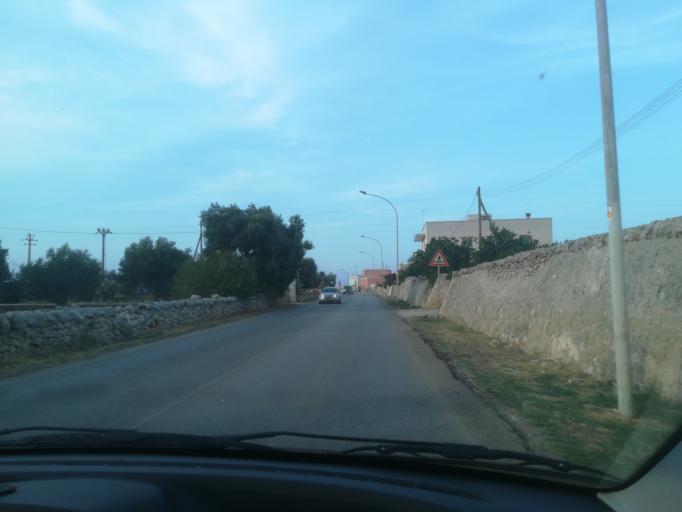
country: IT
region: Apulia
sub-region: Provincia di Bari
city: Monopoli
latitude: 40.9387
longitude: 17.2946
